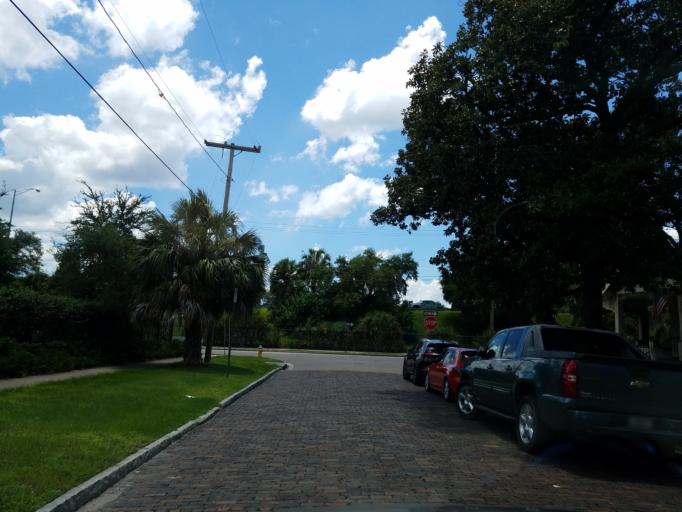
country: US
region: Florida
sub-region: Hillsborough County
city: Tampa
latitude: 27.9435
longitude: -82.4676
